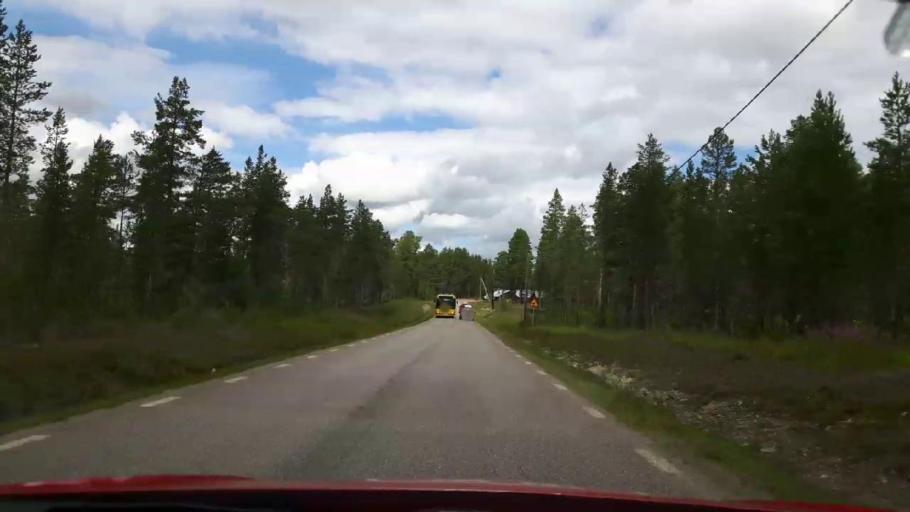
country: NO
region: Hedmark
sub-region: Trysil
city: Innbygda
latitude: 61.8302
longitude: 12.9522
